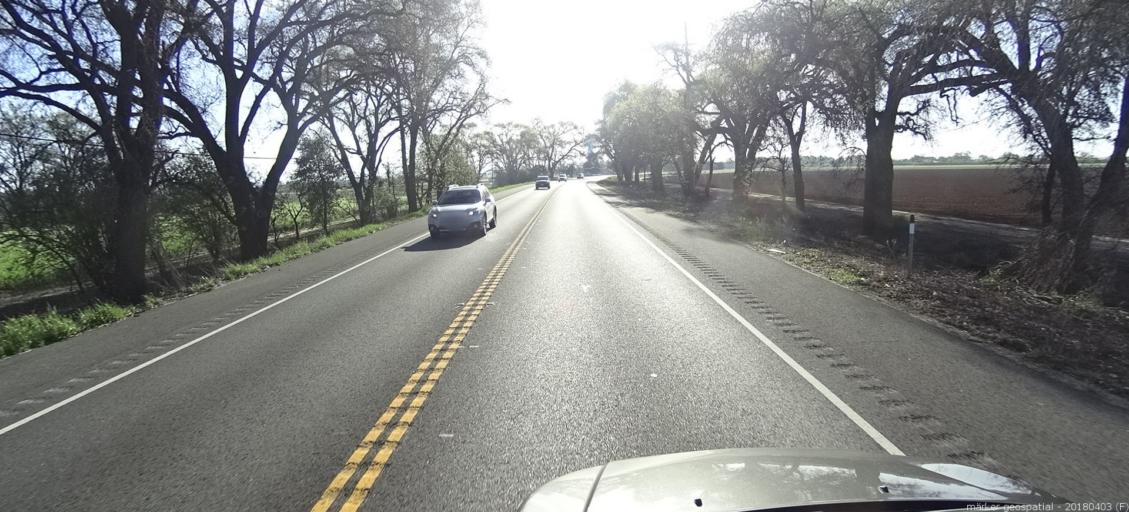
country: US
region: California
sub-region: Sacramento County
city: Rancho Murieta
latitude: 38.4952
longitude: -121.1881
